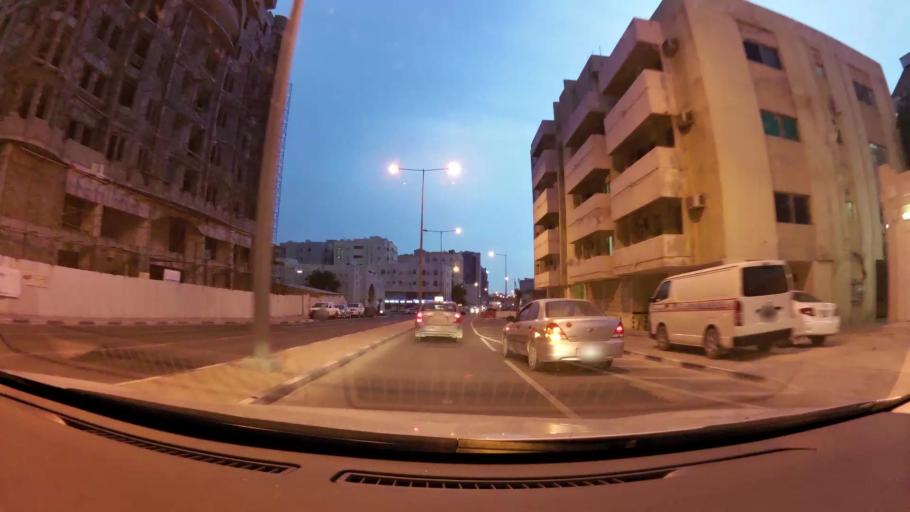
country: QA
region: Baladiyat ad Dawhah
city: Doha
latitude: 25.2708
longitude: 51.5191
